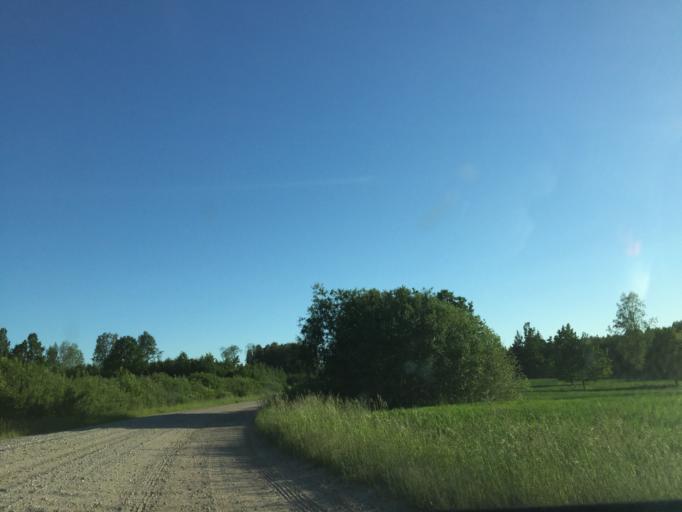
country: LV
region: Broceni
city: Broceni
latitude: 56.8568
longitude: 22.5747
